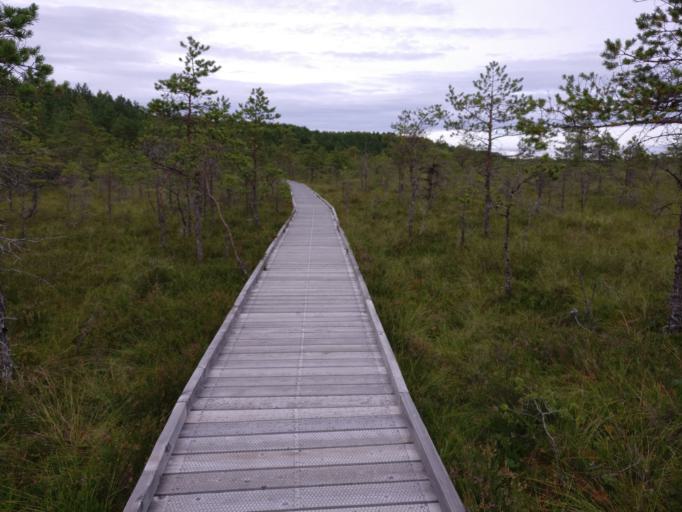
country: EE
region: Paernumaa
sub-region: Vaendra vald (alev)
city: Vandra
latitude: 58.4937
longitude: 24.9860
